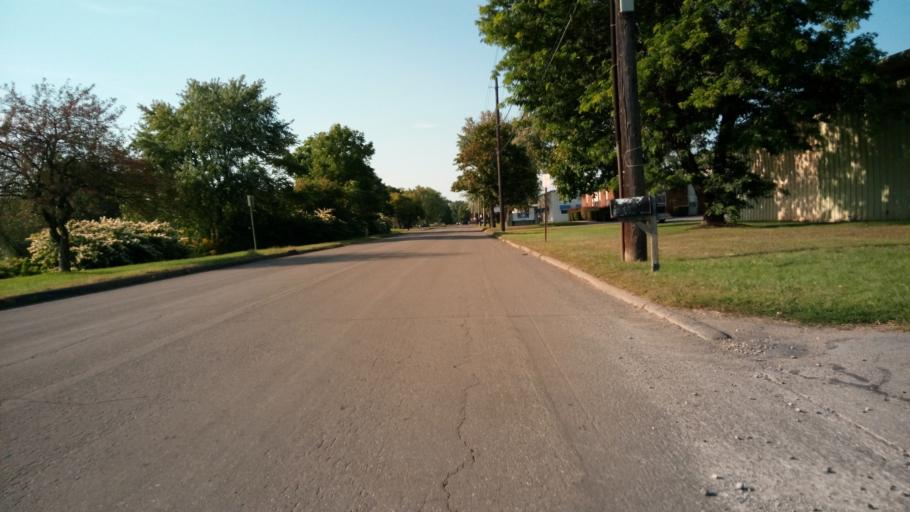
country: US
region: New York
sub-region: Chemung County
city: Elmira
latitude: 42.1068
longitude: -76.8010
